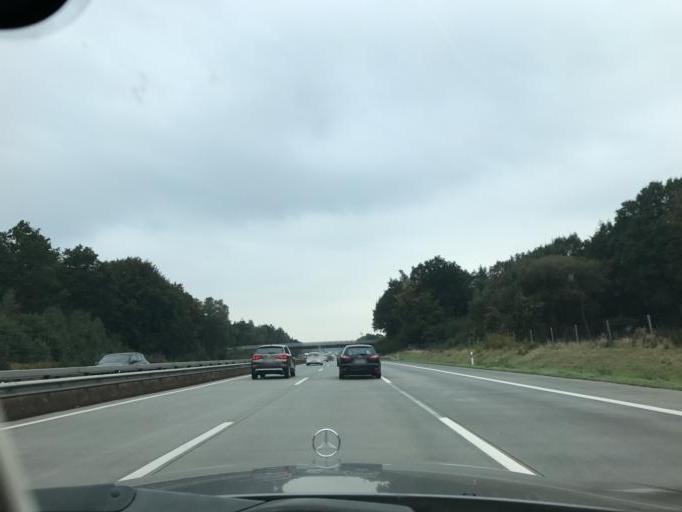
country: DE
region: Lower Saxony
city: Horstedt
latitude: 53.1583
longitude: 9.2378
